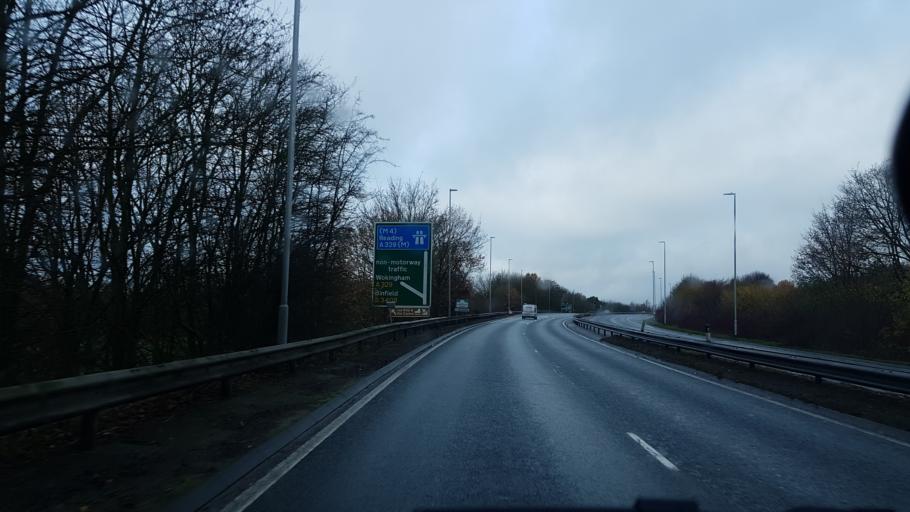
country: GB
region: England
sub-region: Bracknell Forest
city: Binfield
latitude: 51.4097
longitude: -0.7931
